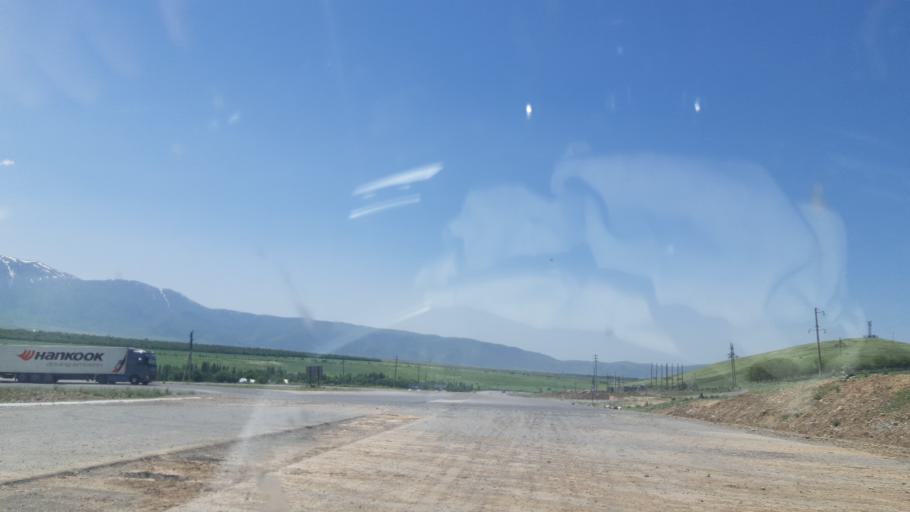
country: KZ
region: Ongtustik Qazaqstan
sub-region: Tulkibas Audany
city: Zhabagly
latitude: 42.5159
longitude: 70.5324
